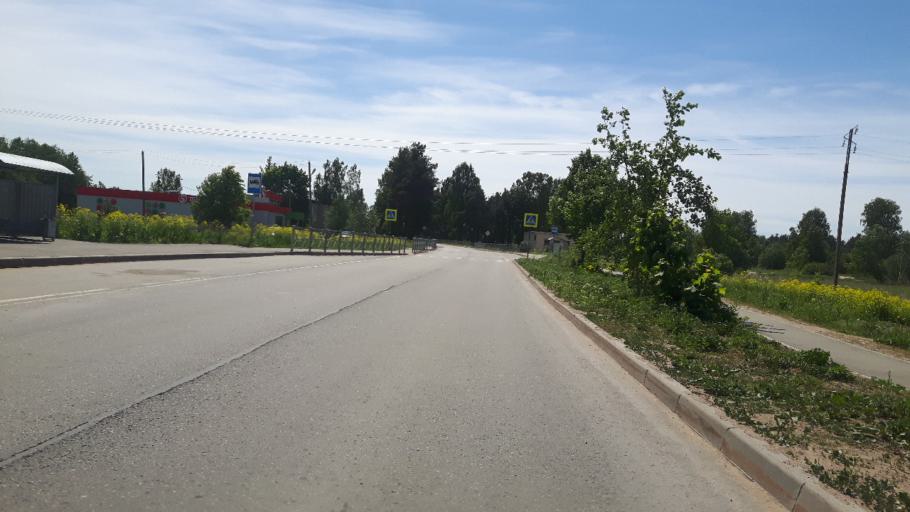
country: RU
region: Leningrad
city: Ust'-Luga
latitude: 59.5798
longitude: 28.1779
